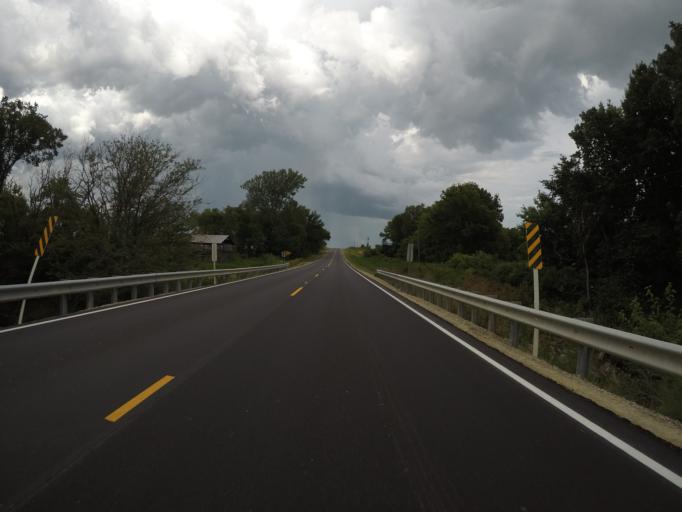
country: US
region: Kansas
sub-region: Marshall County
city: Blue Rapids
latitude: 39.4368
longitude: -96.8290
